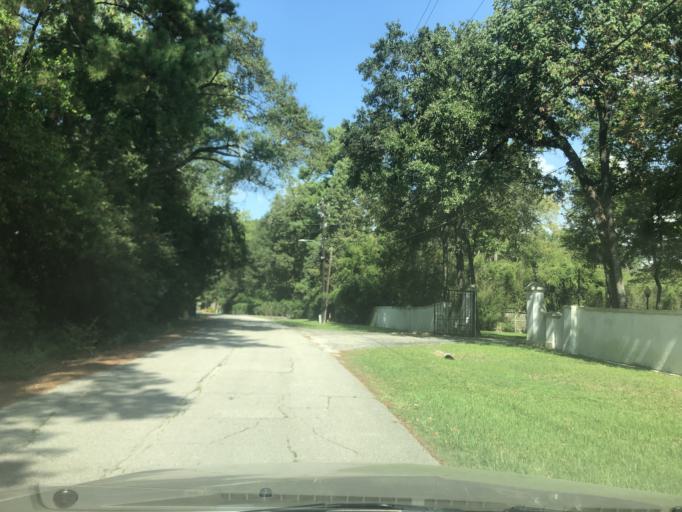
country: US
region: Texas
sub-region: Harris County
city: Bunker Hill Village
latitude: 29.7493
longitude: -95.5423
